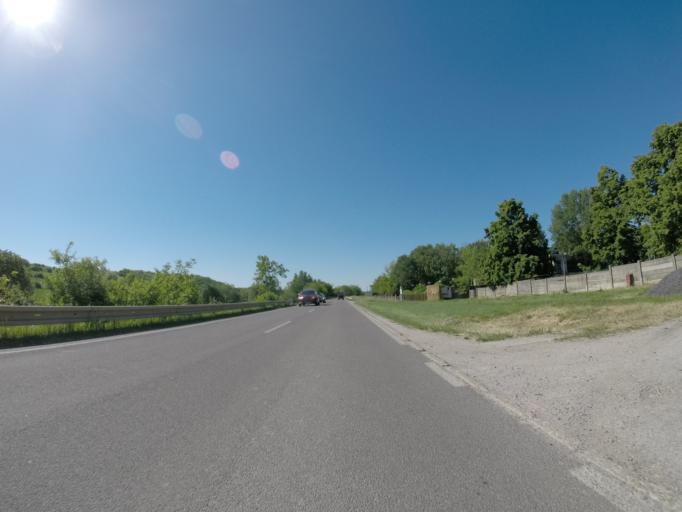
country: SK
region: Trnavsky
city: Hlohovec
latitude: 48.3846
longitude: 17.7970
